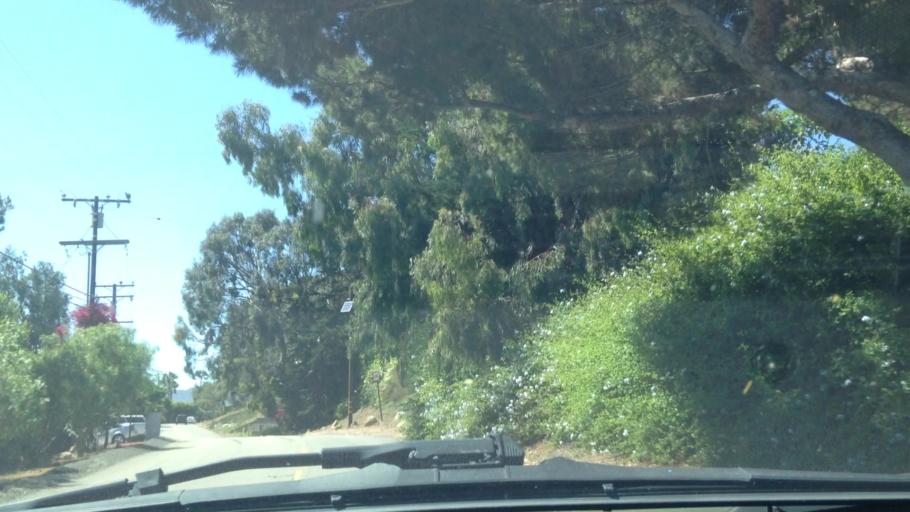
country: US
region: California
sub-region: Los Angeles County
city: Malibu
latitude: 34.0077
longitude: -118.8112
